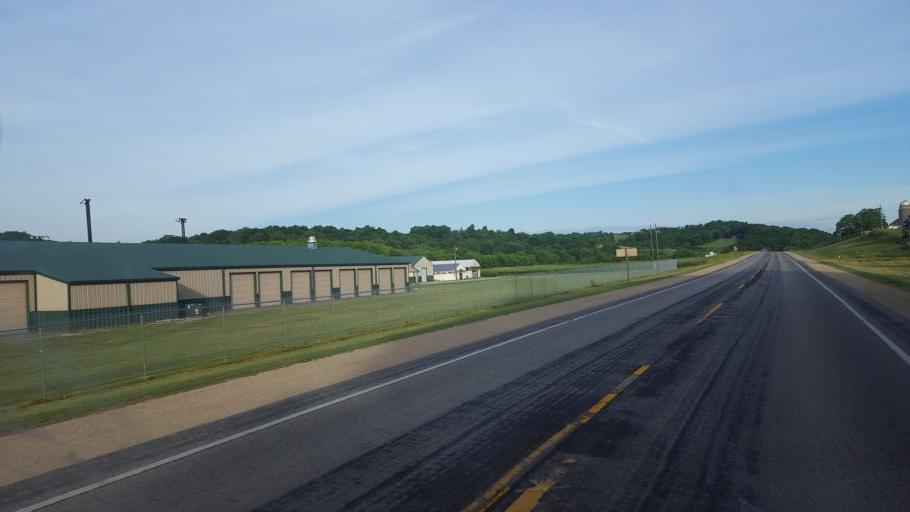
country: US
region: Wisconsin
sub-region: Vernon County
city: Hillsboro
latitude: 43.6531
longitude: -90.3554
